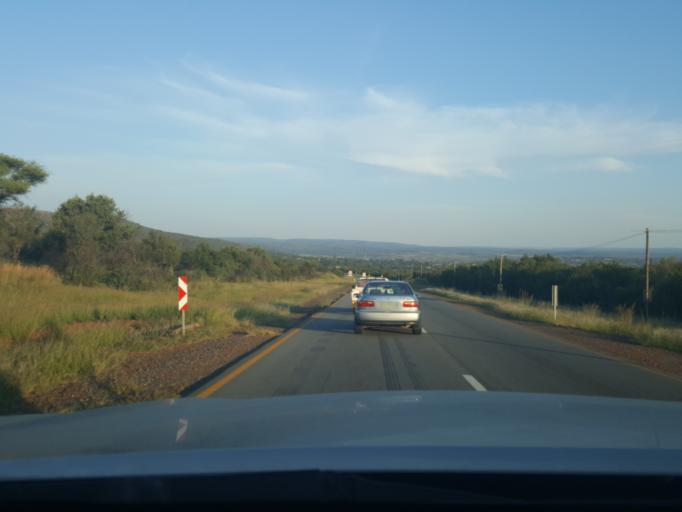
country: ZA
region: North-West
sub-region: Ngaka Modiri Molema District Municipality
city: Zeerust
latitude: -25.5170
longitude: 26.0642
